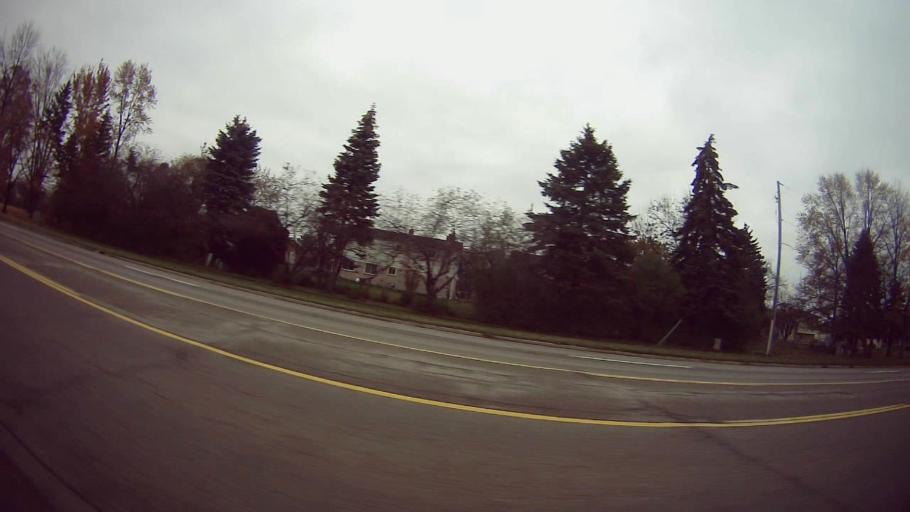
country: US
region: Michigan
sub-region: Oakland County
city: Clawson
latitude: 42.5493
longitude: -83.1024
